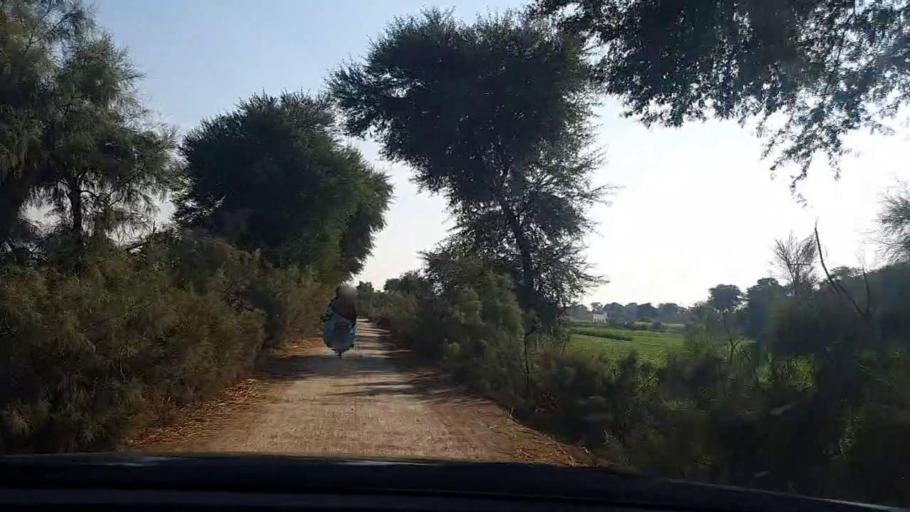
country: PK
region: Sindh
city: Sehwan
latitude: 26.3014
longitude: 67.9878
